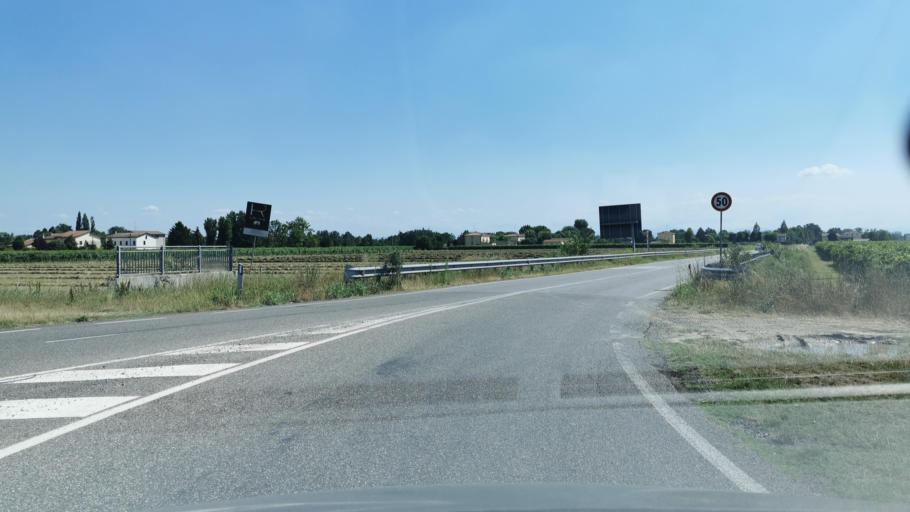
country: IT
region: Emilia-Romagna
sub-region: Provincia di Modena
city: Sam Marino
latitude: 44.7979
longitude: 10.9149
